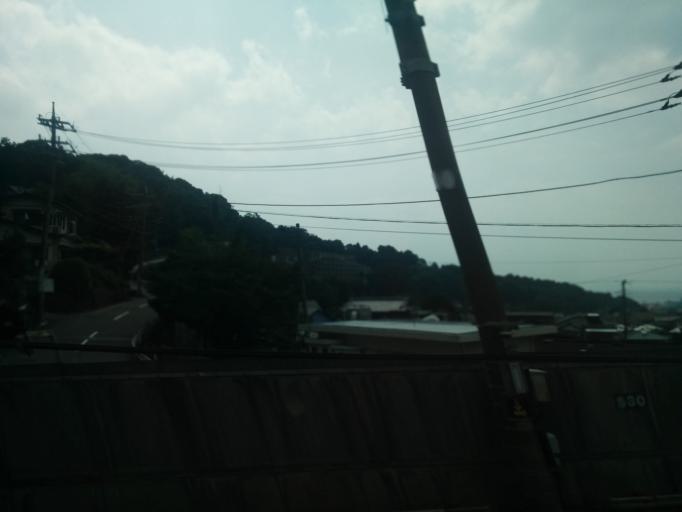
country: JP
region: Kanagawa
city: Yugawara
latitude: 35.1588
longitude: 139.1101
